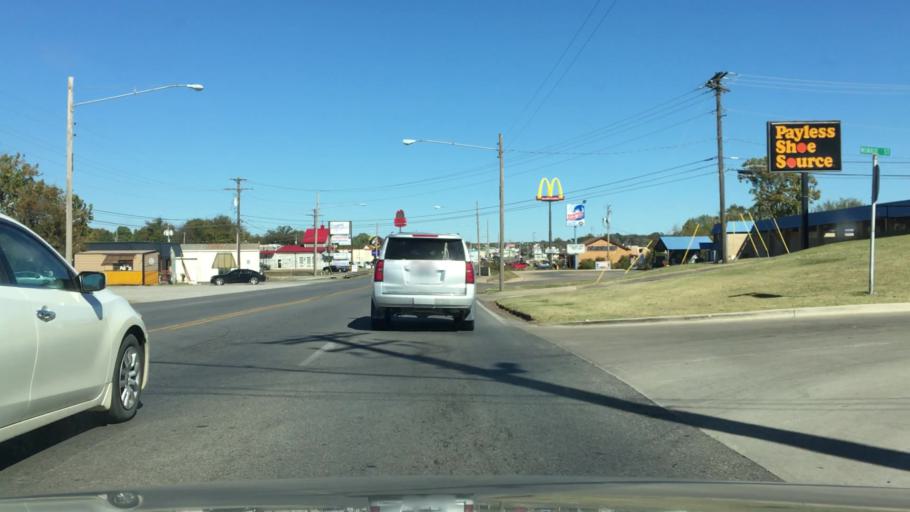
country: US
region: Oklahoma
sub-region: Cherokee County
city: Tahlequah
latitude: 35.8949
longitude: -94.9769
